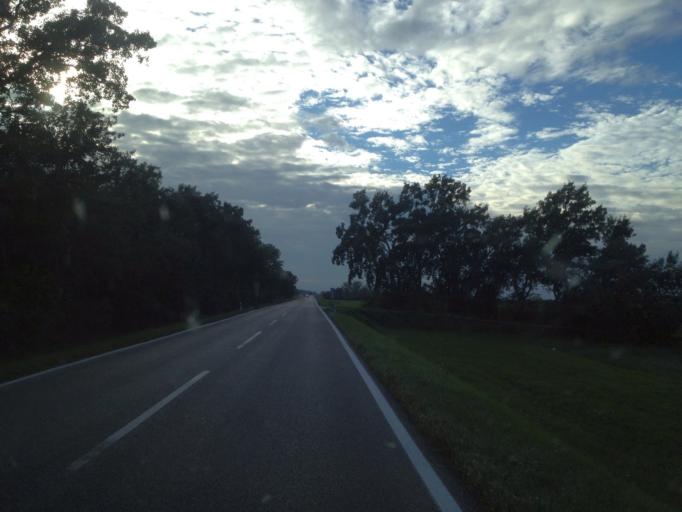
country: HU
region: Komarom-Esztergom
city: Almasfuzito
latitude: 47.7424
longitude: 18.2701
